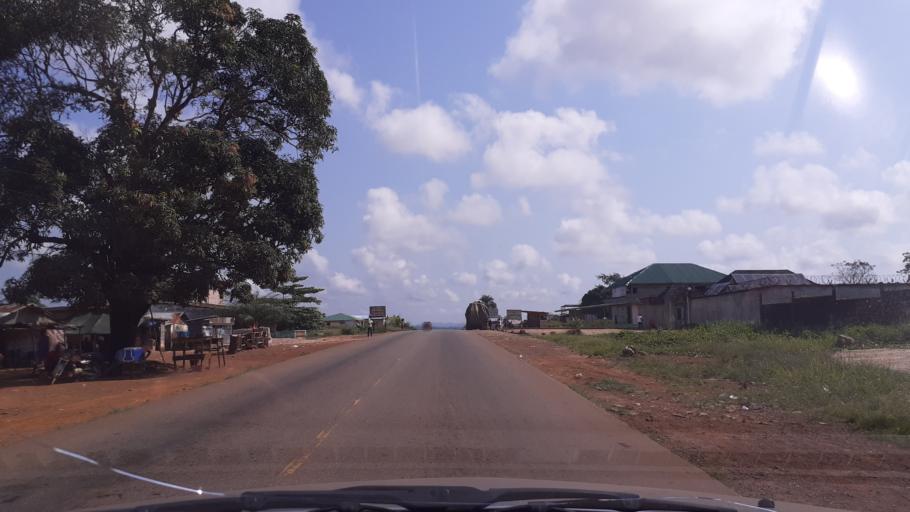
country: LR
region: Montserrado
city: Bensonville City
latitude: 6.2252
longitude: -10.5343
